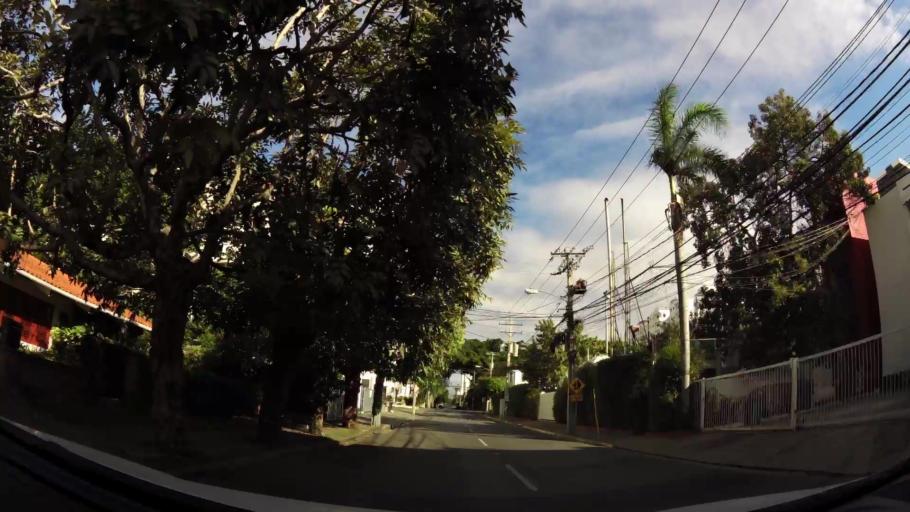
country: DO
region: Nacional
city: La Julia
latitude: 18.4750
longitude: -69.9382
